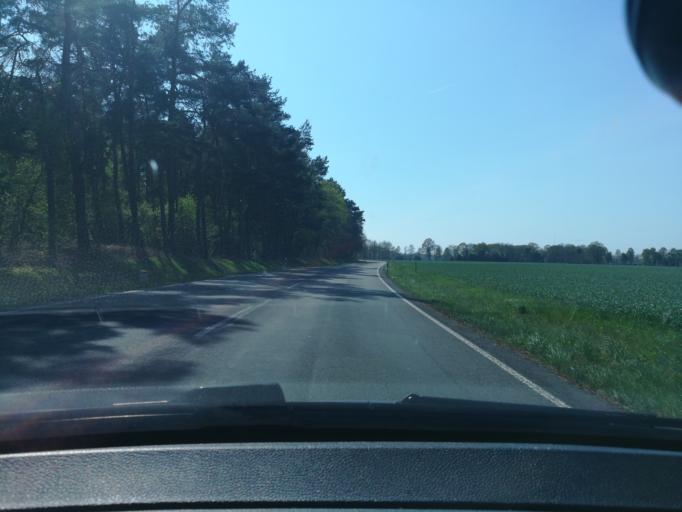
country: DE
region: North Rhine-Westphalia
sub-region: Regierungsbezirk Detmold
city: Harsewinkel
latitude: 52.0175
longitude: 8.2364
